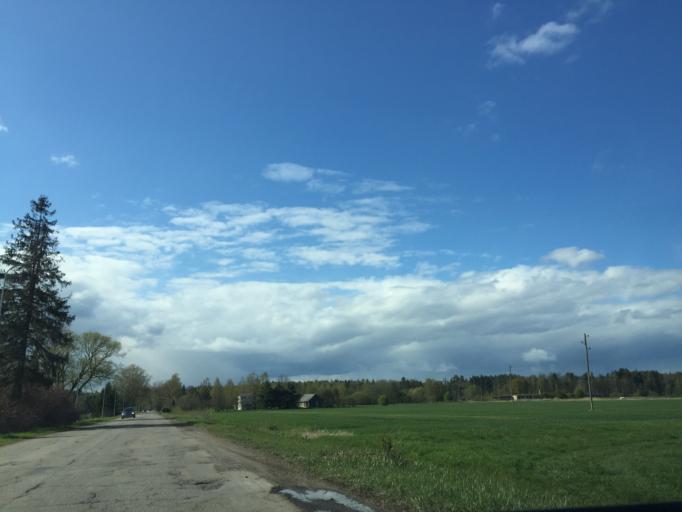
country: LV
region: Jelgava
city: Jelgava
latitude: 56.5629
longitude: 23.7633
